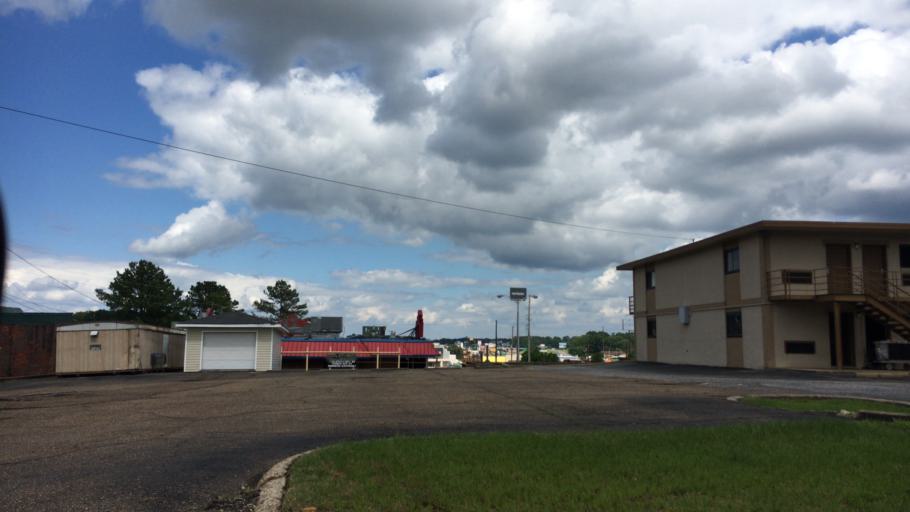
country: US
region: Louisiana
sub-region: Lincoln Parish
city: Ruston
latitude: 32.5421
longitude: -92.6394
